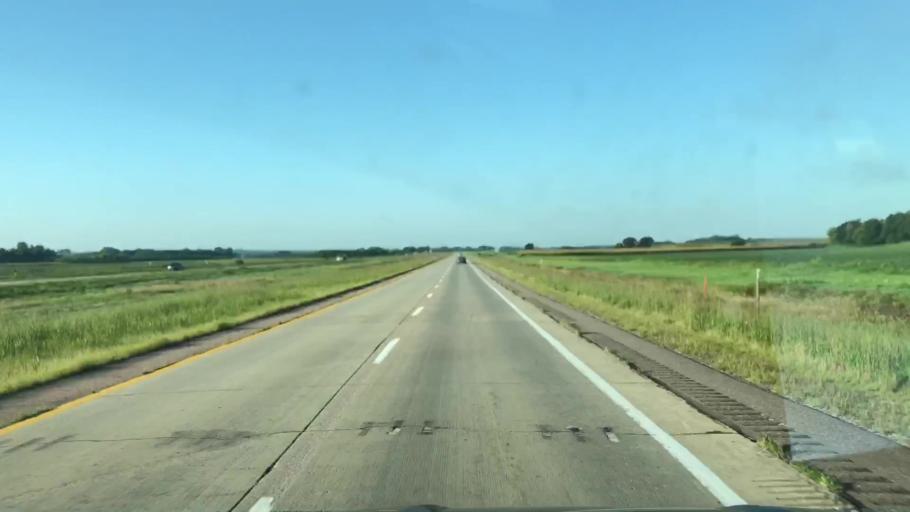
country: US
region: Iowa
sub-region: Sioux County
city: Orange City
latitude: 42.8949
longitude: -96.0903
